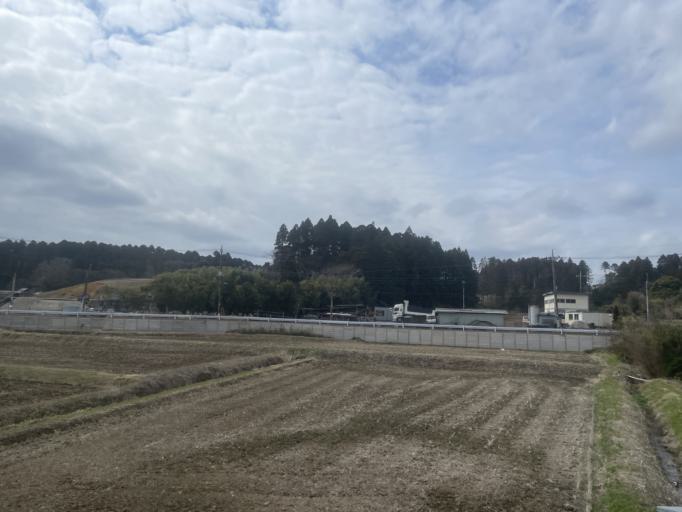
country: JP
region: Chiba
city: Yachimata
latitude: 35.6396
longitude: 140.3508
